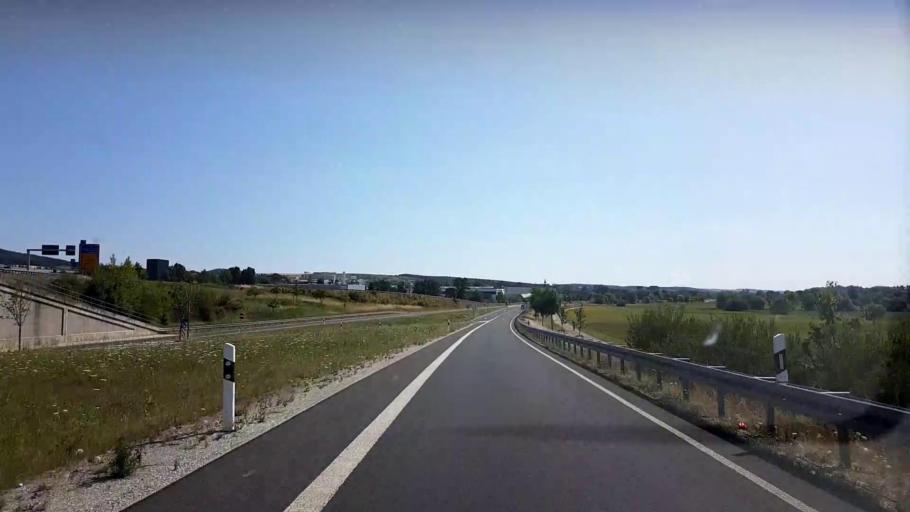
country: DE
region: Bavaria
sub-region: Upper Franconia
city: Grossheirath
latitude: 50.1904
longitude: 10.9553
